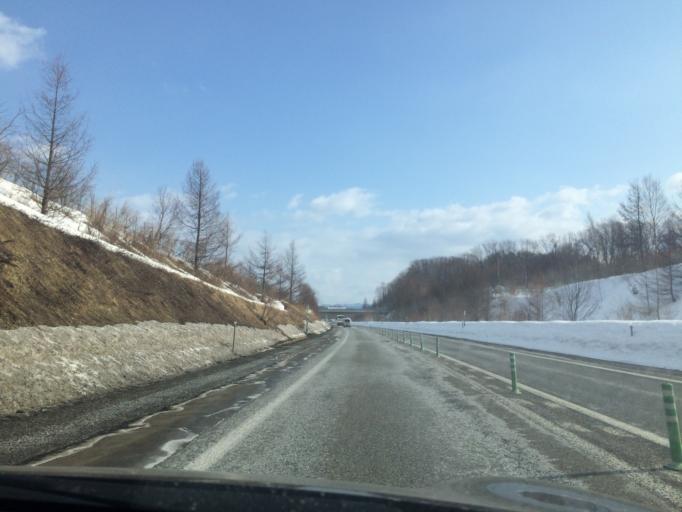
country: JP
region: Hokkaido
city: Chitose
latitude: 42.8946
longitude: 141.8315
